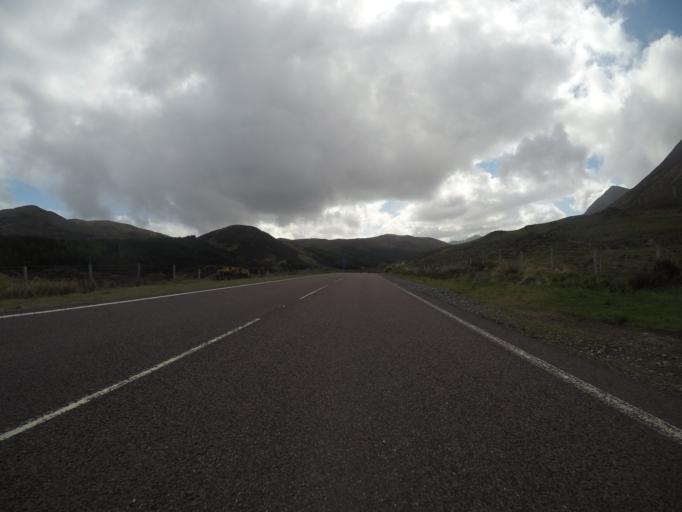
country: GB
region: Scotland
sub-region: Highland
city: Portree
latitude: 57.3068
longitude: -6.0920
